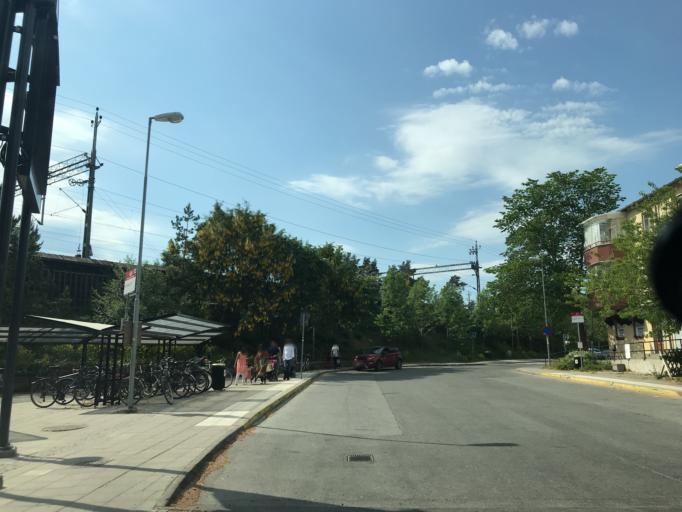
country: SE
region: Stockholm
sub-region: Stockholms Kommun
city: Kista
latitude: 59.4096
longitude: 17.9627
